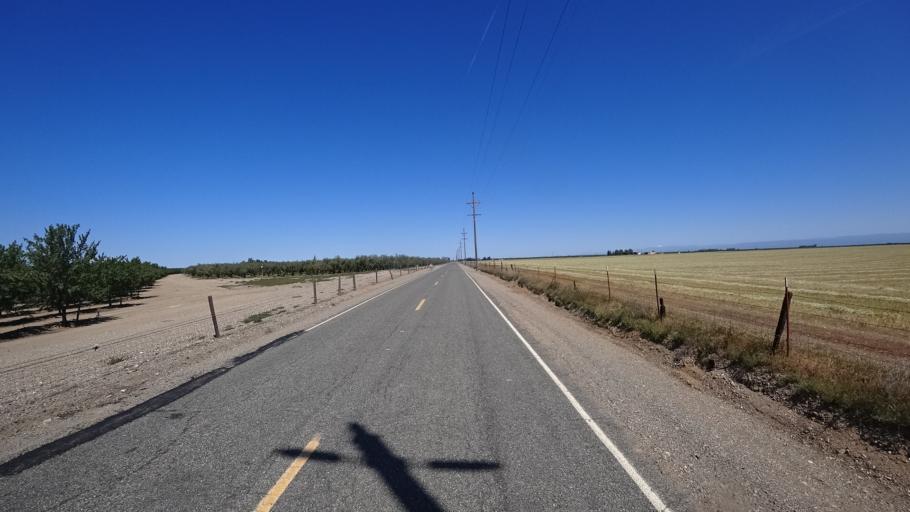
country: US
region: California
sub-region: Glenn County
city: Orland
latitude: 39.6559
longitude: -122.1785
